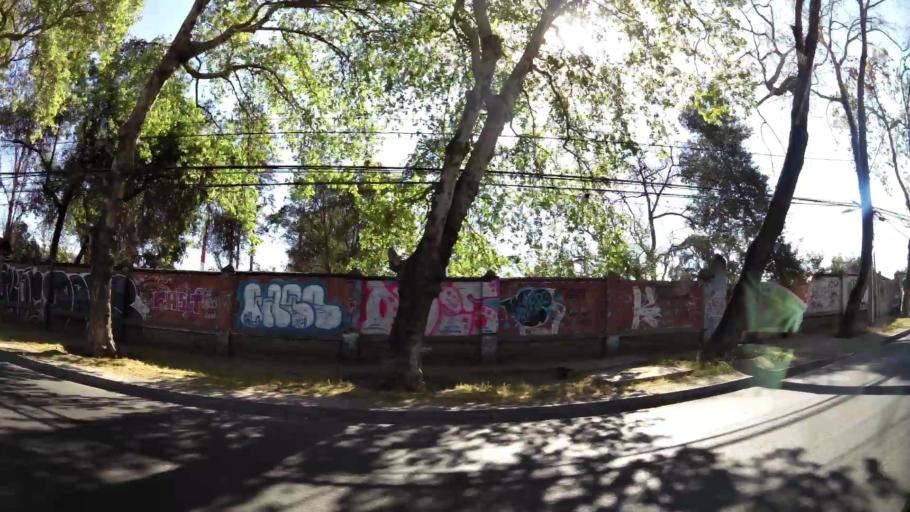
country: CL
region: Santiago Metropolitan
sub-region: Provincia de Maipo
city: San Bernardo
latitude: -33.6115
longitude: -70.6970
